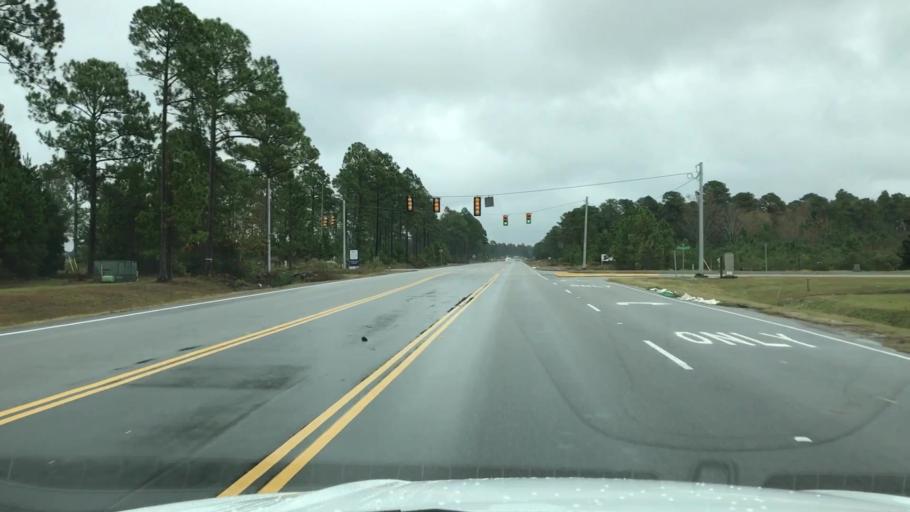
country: US
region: South Carolina
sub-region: Horry County
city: Forestbrook
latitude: 33.7591
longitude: -78.9007
